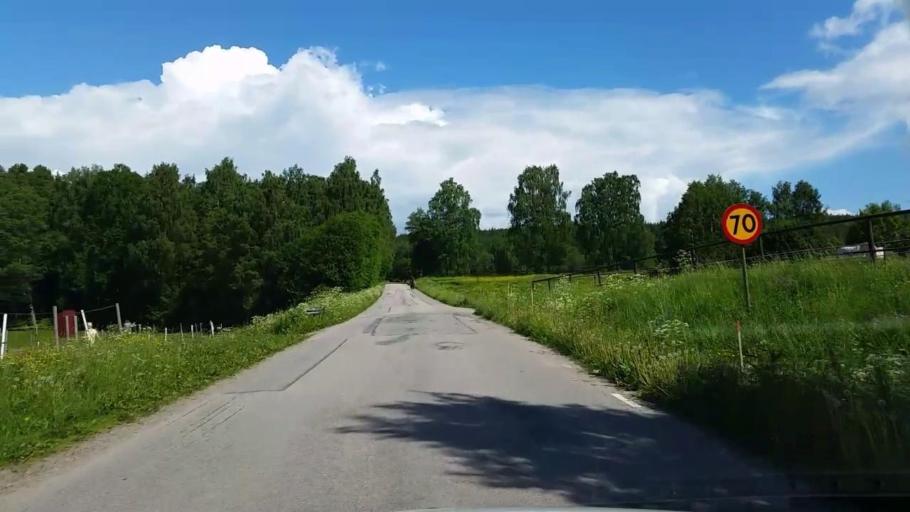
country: SE
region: Vaestmanland
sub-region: Fagersta Kommun
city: Fagersta
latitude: 59.9761
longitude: 15.7435
